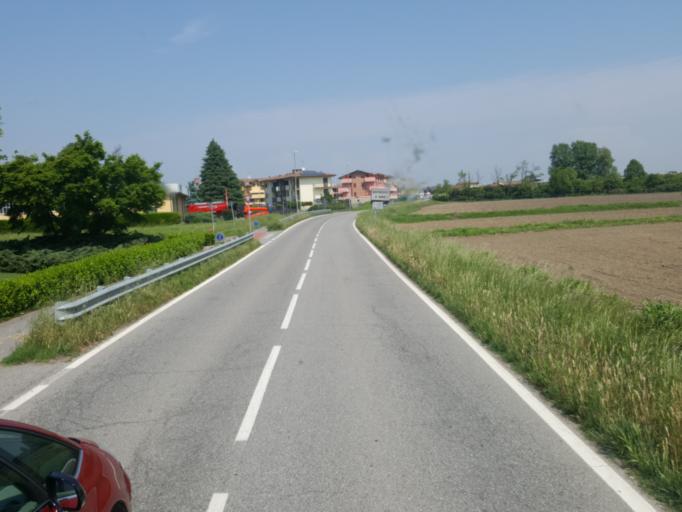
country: IT
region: Lombardy
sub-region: Provincia di Lodi
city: Boffalora d'Adda
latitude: 45.3535
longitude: 9.4962
